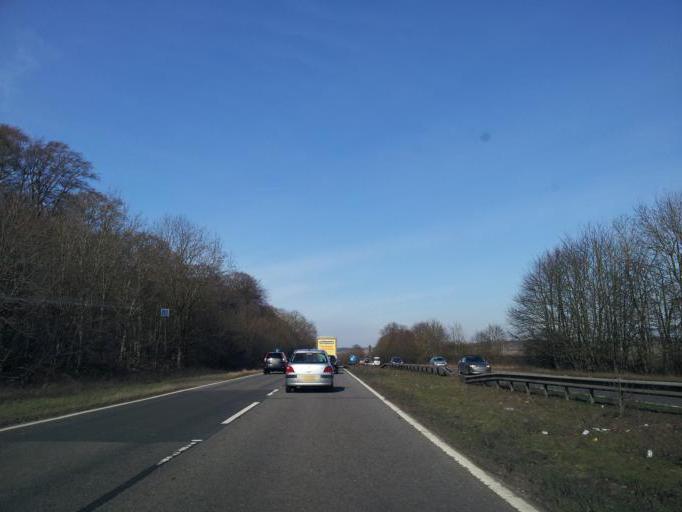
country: GB
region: England
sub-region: Lincolnshire
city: Grantham
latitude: 52.8462
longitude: -0.6281
